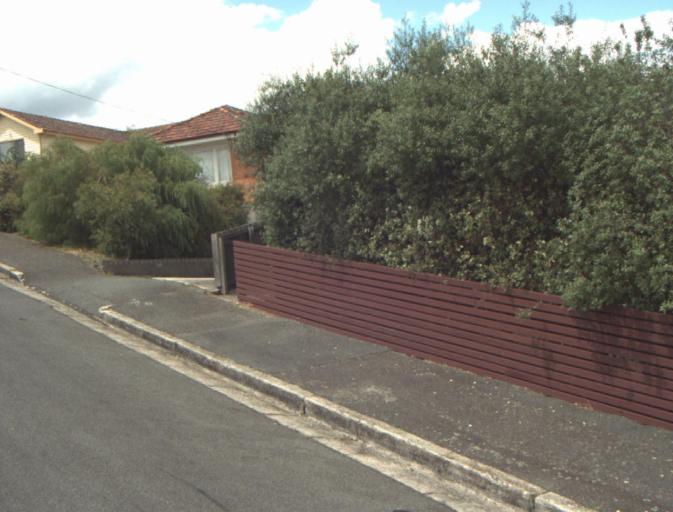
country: AU
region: Tasmania
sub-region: Launceston
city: Newnham
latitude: -41.4090
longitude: 147.1436
